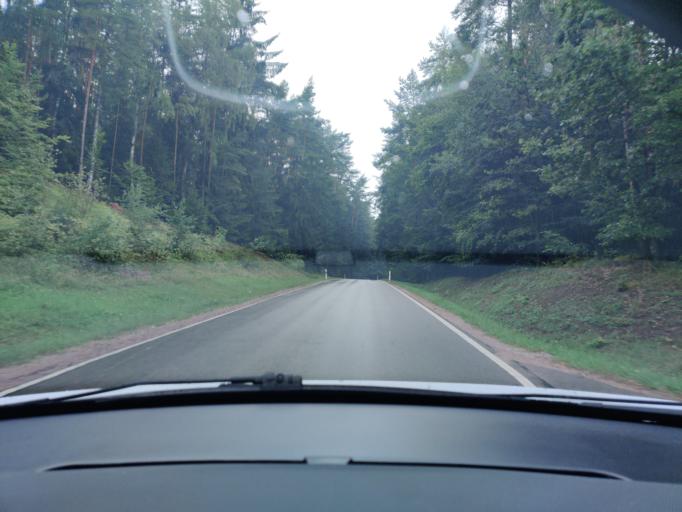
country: DE
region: Bavaria
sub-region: Upper Palatinate
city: Pfreimd
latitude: 49.5010
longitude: 12.1572
